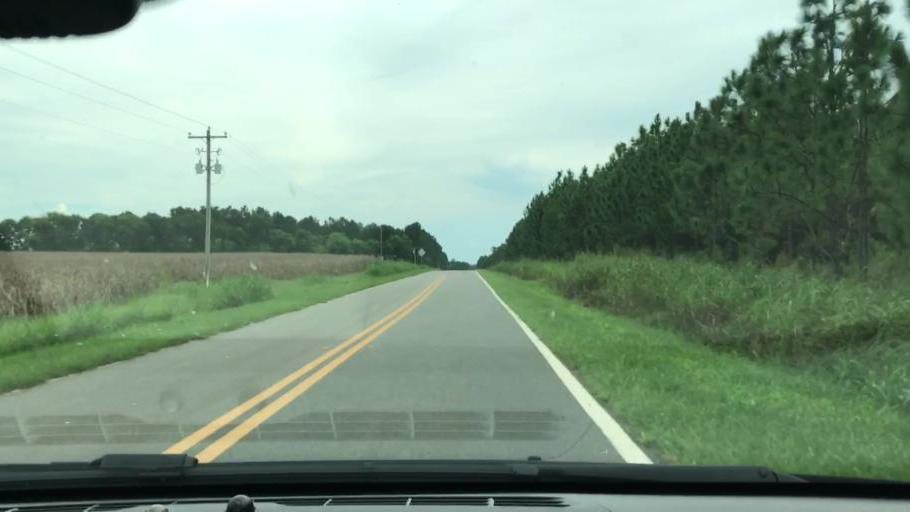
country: US
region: Georgia
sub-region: Early County
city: Blakely
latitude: 31.4263
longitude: -84.9247
